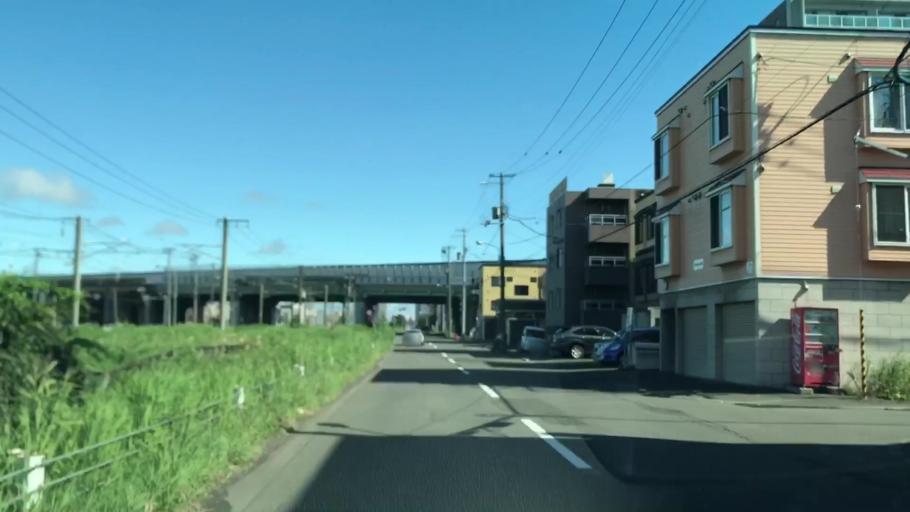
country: JP
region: Hokkaido
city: Sapporo
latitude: 43.0947
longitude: 141.2853
